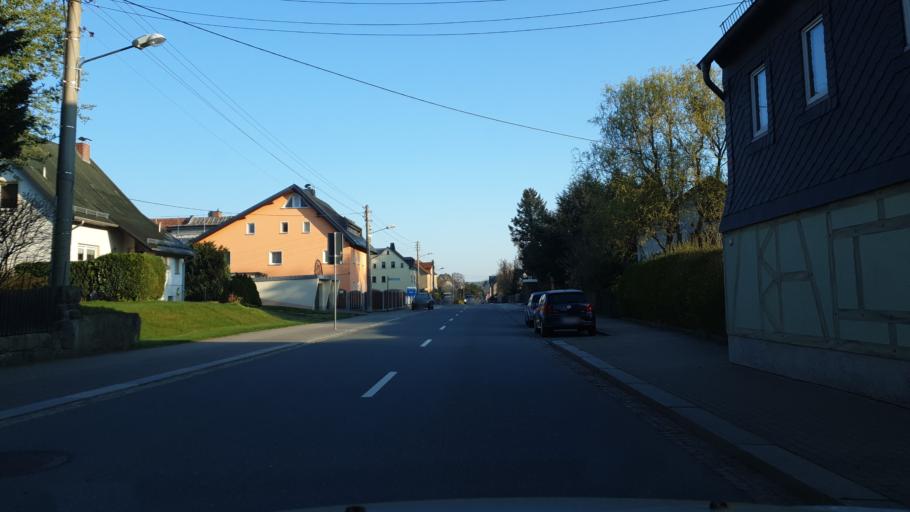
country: DE
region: Saxony
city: Oberlungwitz
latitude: 50.7664
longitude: 12.7067
